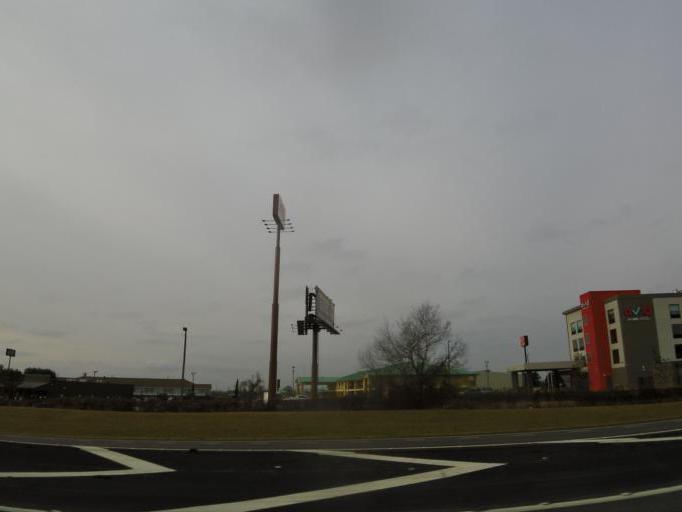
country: US
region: Alabama
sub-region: Elmore County
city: Millbrook
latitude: 32.4900
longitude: -86.4107
